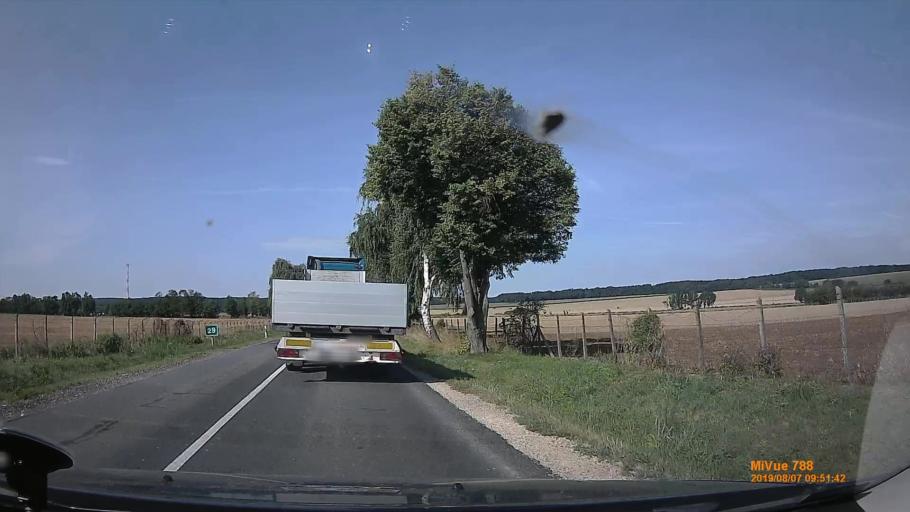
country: HU
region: Zala
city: Pacsa
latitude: 46.7389
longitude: 16.9069
